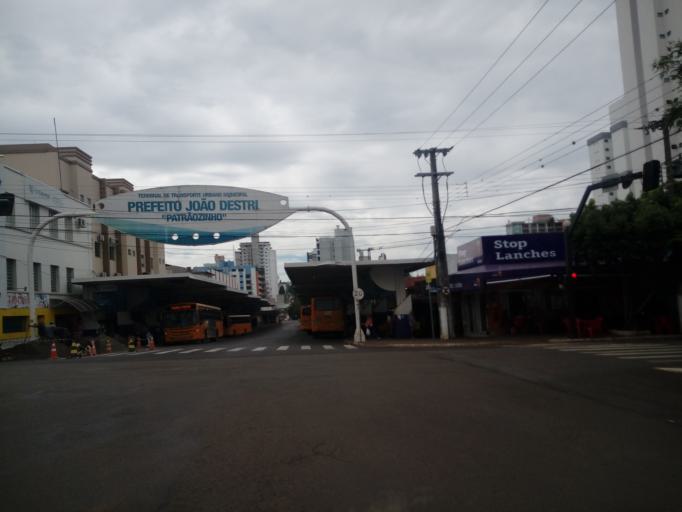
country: BR
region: Santa Catarina
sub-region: Chapeco
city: Chapeco
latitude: -27.1066
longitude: -52.6139
